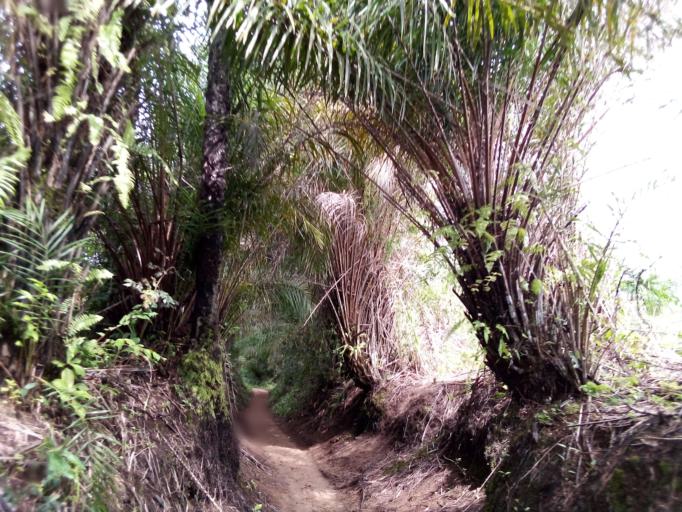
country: SL
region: Southern Province
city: Bonthe
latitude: 7.5106
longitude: -12.5517
